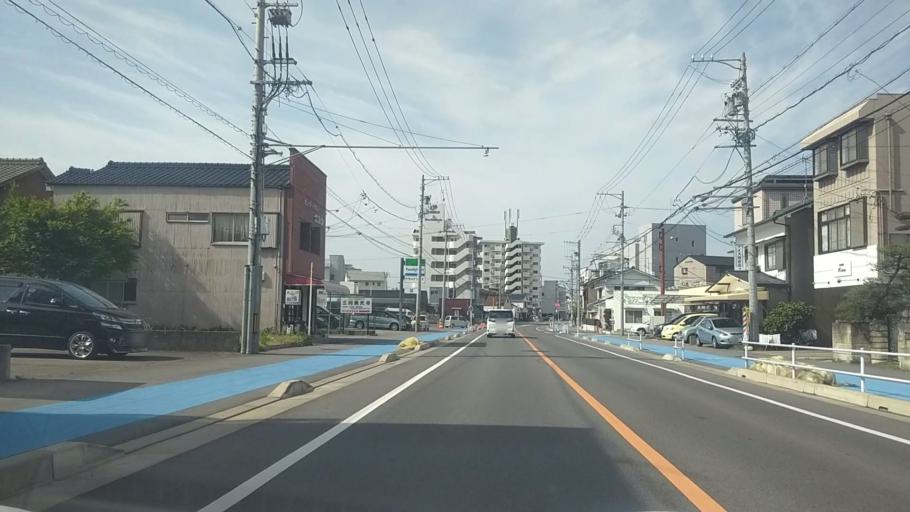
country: JP
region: Aichi
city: Okazaki
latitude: 34.9521
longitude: 137.1622
